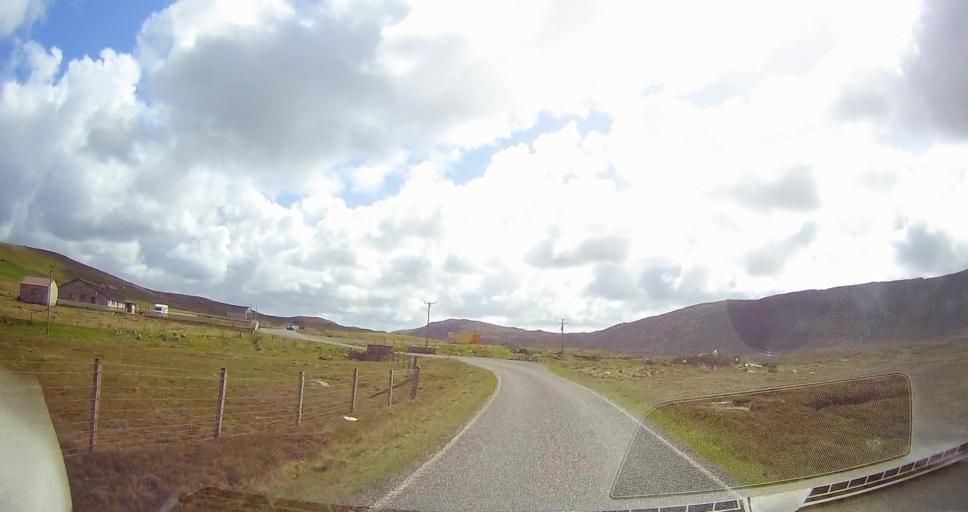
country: GB
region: Scotland
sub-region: Shetland Islands
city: Lerwick
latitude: 60.5726
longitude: -1.3322
